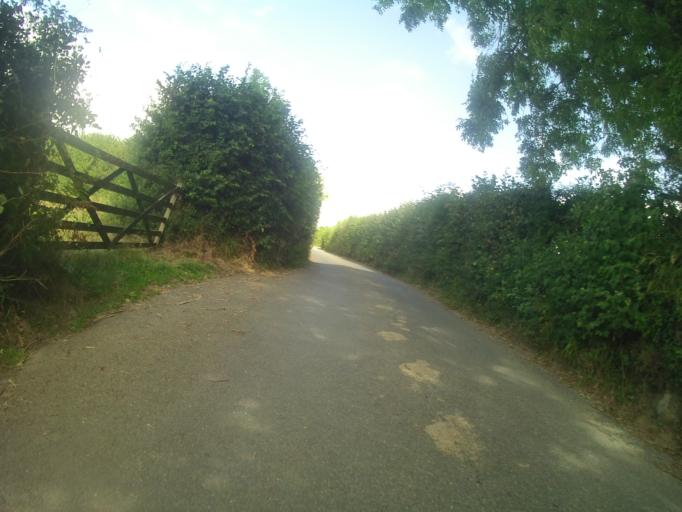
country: GB
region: England
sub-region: Devon
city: Buckfastleigh
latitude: 50.5060
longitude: -3.8183
